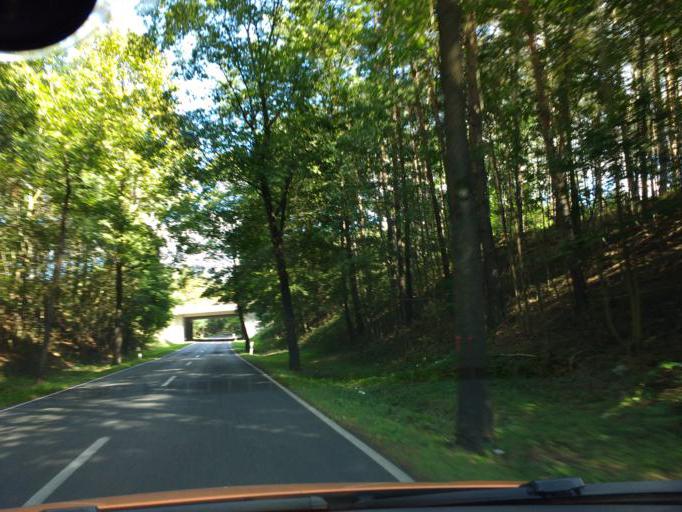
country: DE
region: Brandenburg
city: Bestensee
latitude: 52.2160
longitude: 13.5997
